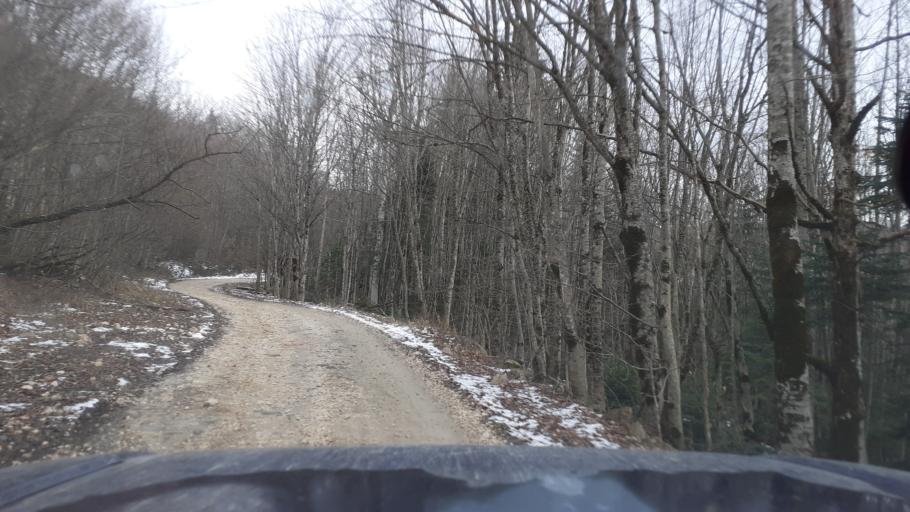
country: RU
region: Krasnodarskiy
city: Neftegorsk
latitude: 44.0783
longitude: 39.7508
